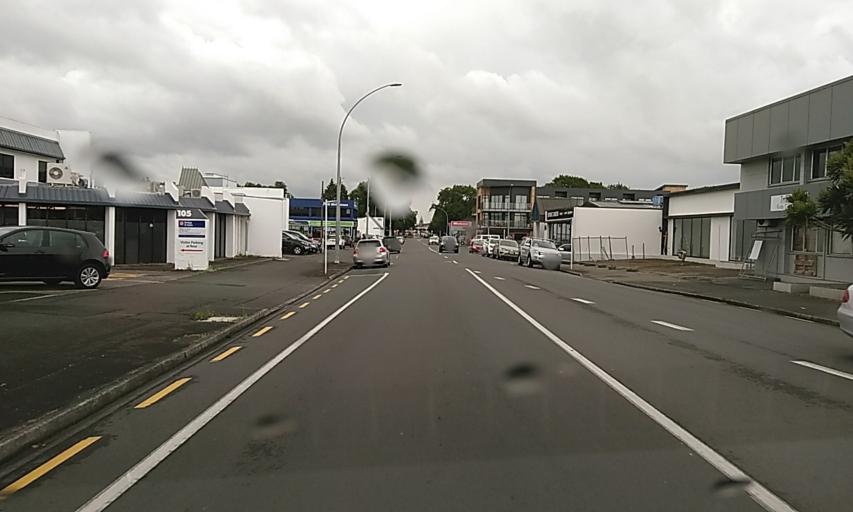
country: NZ
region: Waikato
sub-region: Hamilton City
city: Hamilton
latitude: -37.7829
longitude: 175.2753
